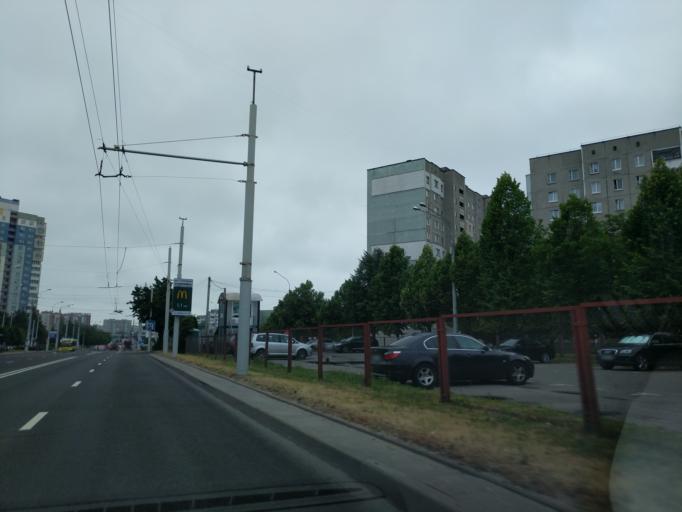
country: BY
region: Minsk
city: Novoye Medvezhino
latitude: 53.8672
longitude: 27.4710
